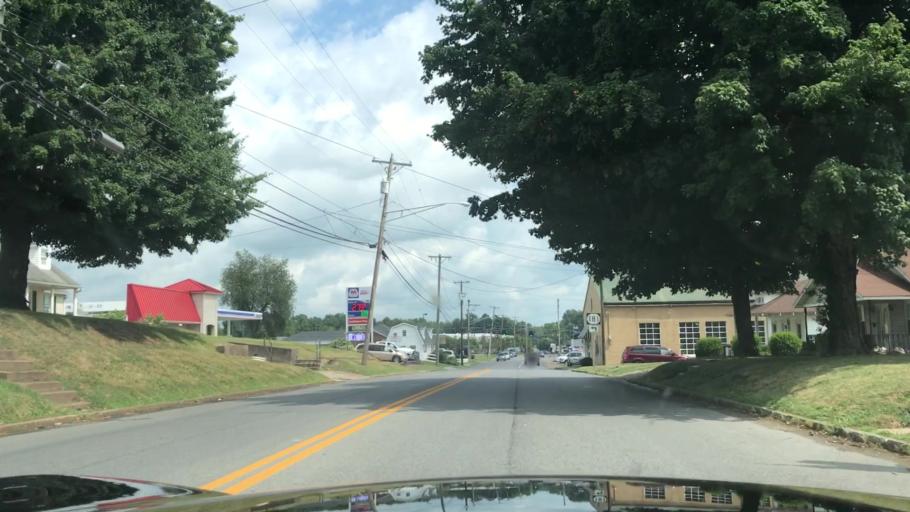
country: US
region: Kentucky
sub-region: Muhlenberg County
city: Greenville
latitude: 37.2111
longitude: -87.1805
